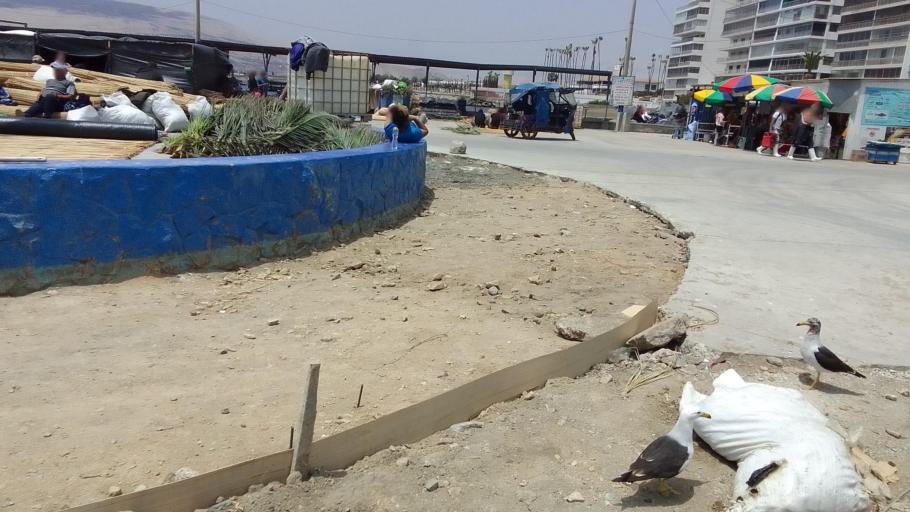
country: PE
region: Lima
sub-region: Lima
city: Santa Rosa
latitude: -11.7730
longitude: -77.1765
